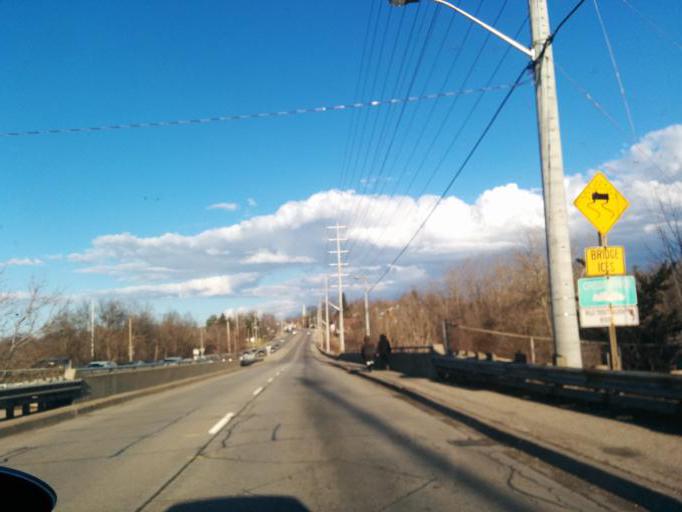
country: CA
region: Ontario
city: Mississauga
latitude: 43.5429
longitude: -79.6583
